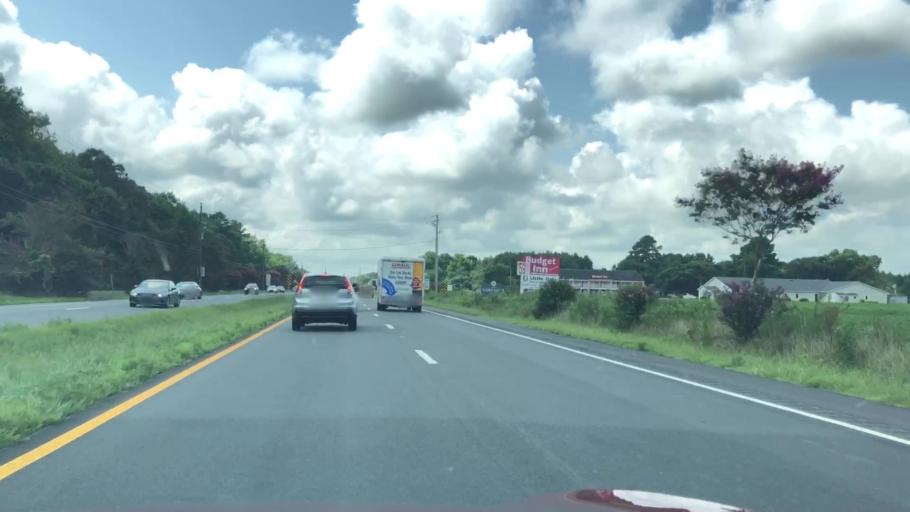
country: US
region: Virginia
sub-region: Northampton County
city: Exmore
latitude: 37.4839
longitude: -75.8528
